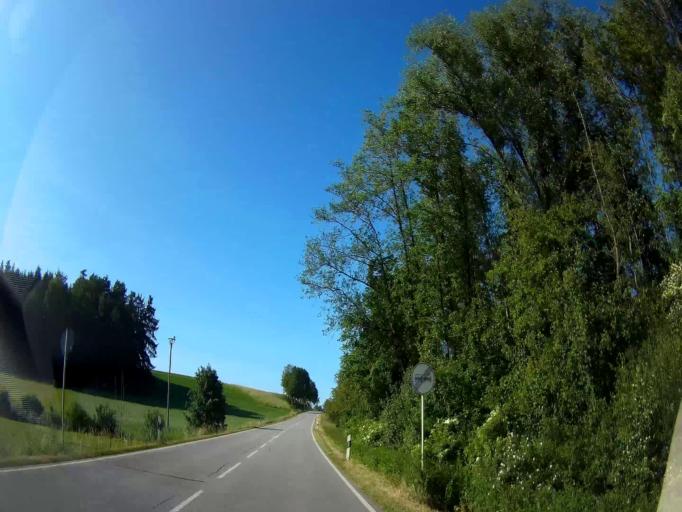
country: DE
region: Bavaria
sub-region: Lower Bavaria
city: Zeilarn
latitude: 48.3094
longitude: 12.8287
